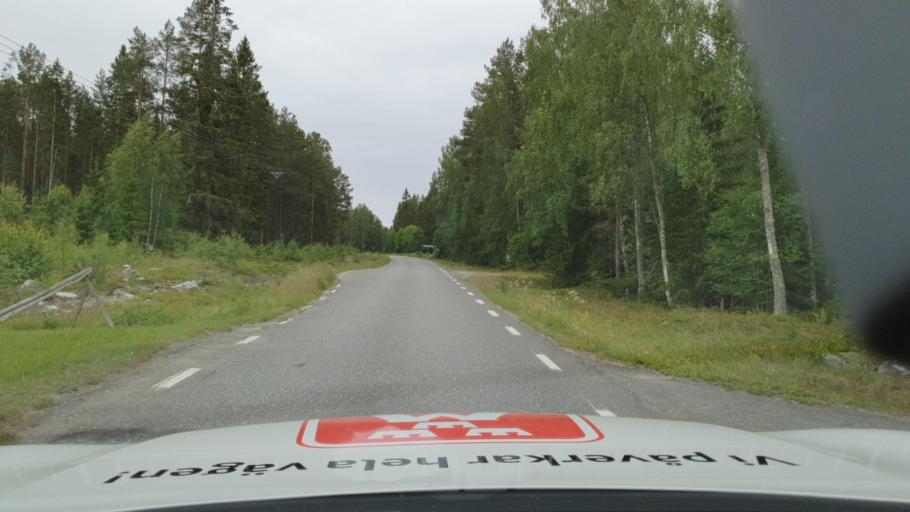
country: SE
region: Vaesterbotten
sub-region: Nordmalings Kommun
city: Nordmaling
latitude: 63.4379
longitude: 19.4696
